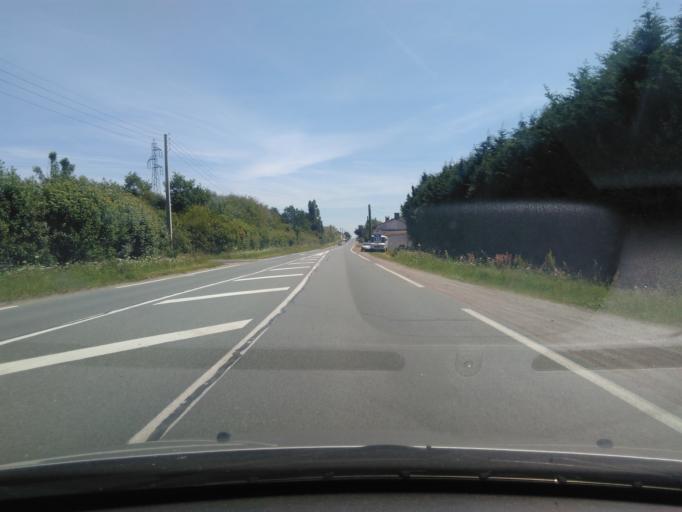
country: FR
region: Pays de la Loire
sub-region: Departement de la Vendee
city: La Roche-sur-Yon
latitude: 46.6435
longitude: -1.4094
